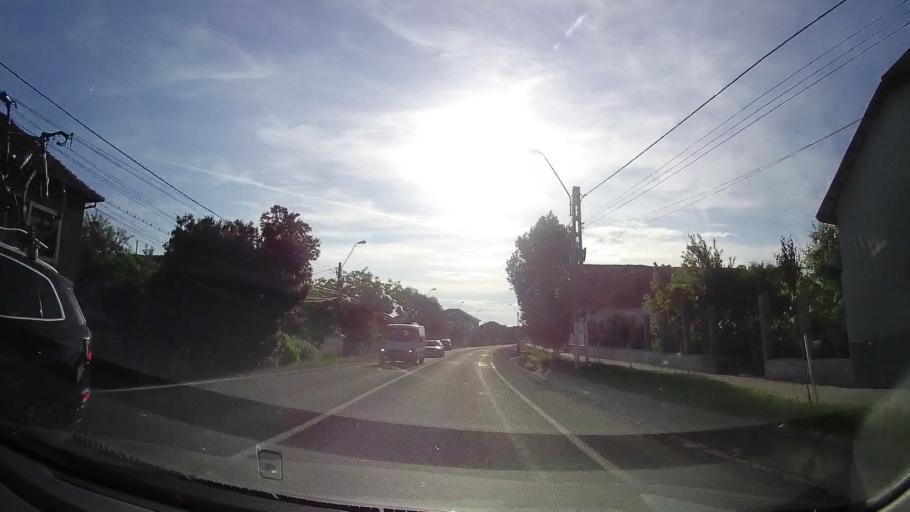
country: RO
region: Timis
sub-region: Oras Recas
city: Recas
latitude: 45.7982
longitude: 21.4987
